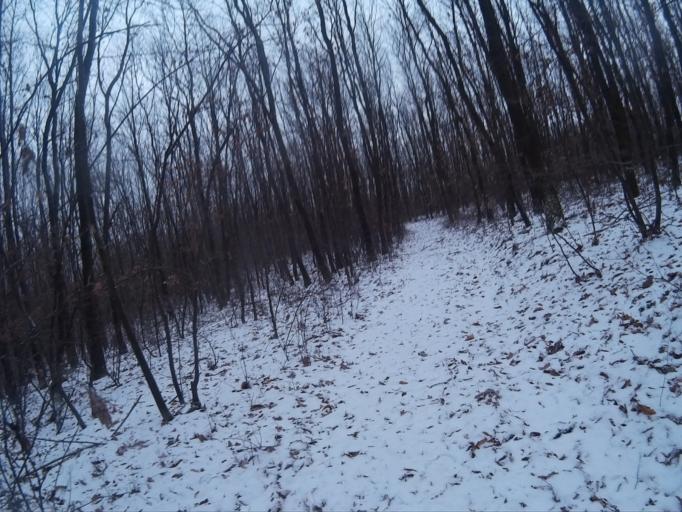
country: HU
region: Borsod-Abauj-Zemplen
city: Szendro
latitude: 48.3897
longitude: 20.8965
